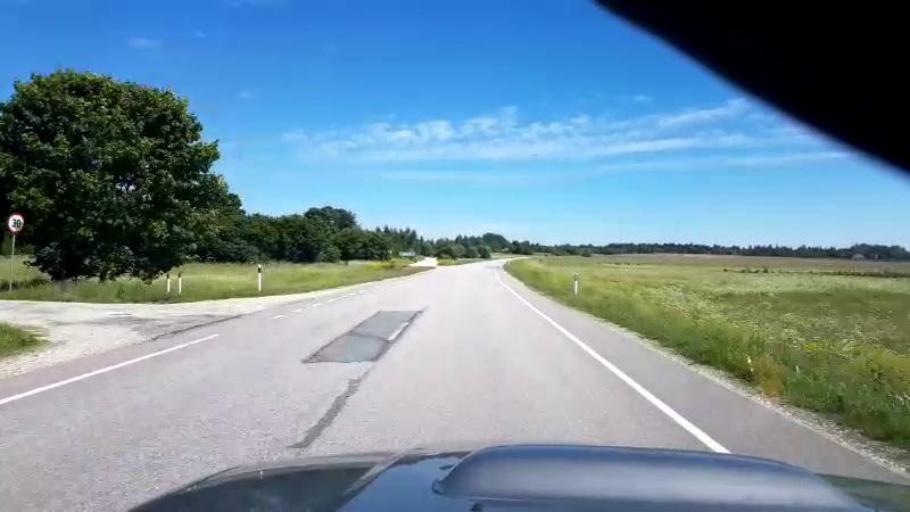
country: EE
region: Jaervamaa
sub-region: Koeru vald
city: Koeru
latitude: 58.9786
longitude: 26.0870
